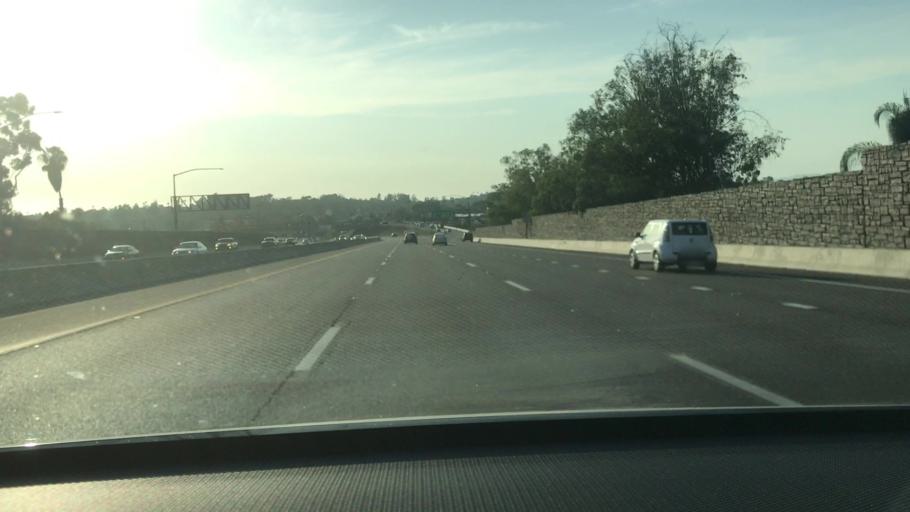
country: US
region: California
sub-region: San Diego County
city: Vista
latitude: 33.1931
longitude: -117.2452
